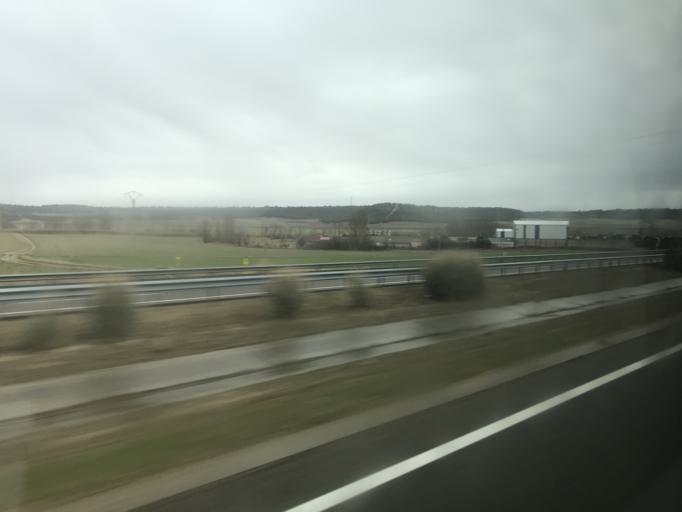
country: ES
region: Castille and Leon
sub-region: Provincia de Palencia
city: Villalobon
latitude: 42.0243
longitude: -4.5145
